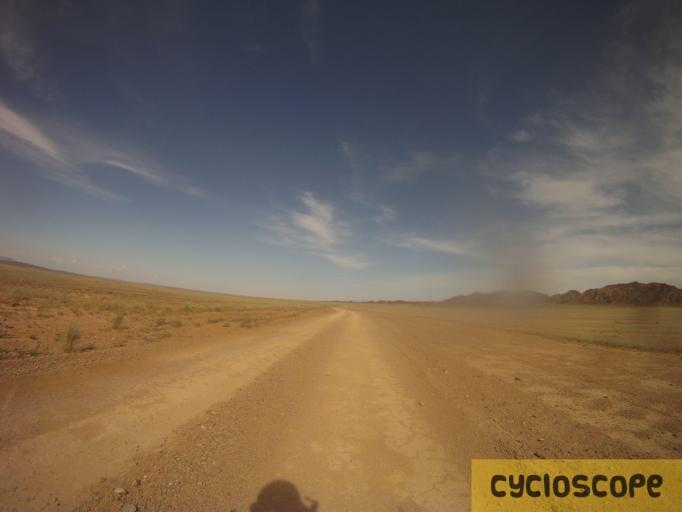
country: KZ
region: Almaty Oblysy
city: Kegen
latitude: 43.3563
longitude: 78.9536
